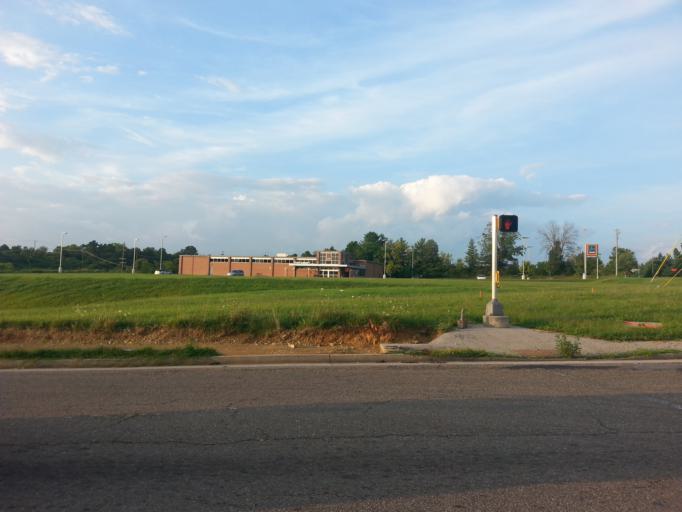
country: US
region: Tennessee
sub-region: Knox County
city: Knoxville
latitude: 36.0832
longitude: -83.9350
